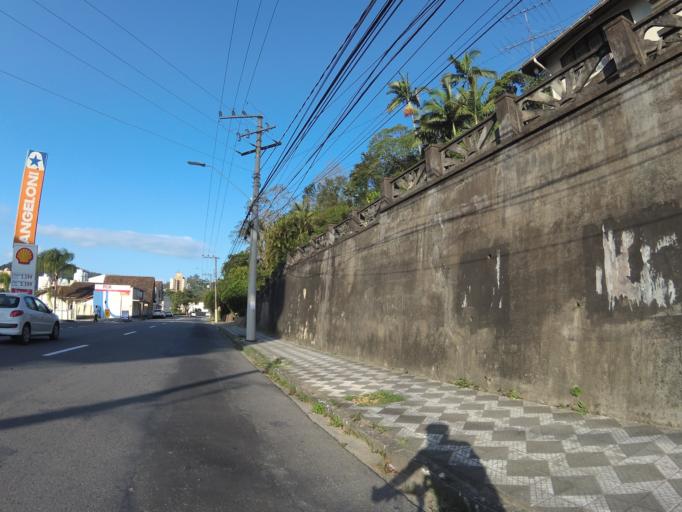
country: BR
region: Santa Catarina
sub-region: Blumenau
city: Blumenau
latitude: -26.9151
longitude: -49.0803
